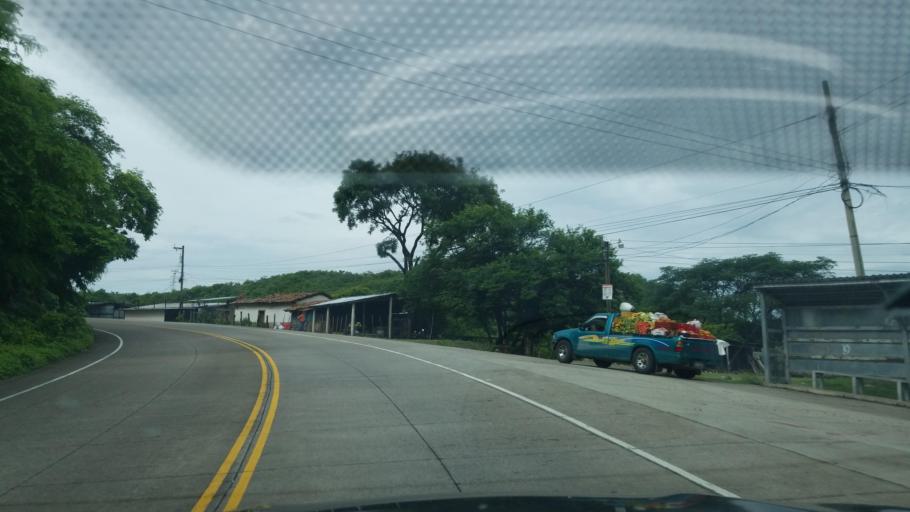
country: HN
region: Francisco Morazan
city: El Porvenir
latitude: 13.6838
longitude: -87.3569
